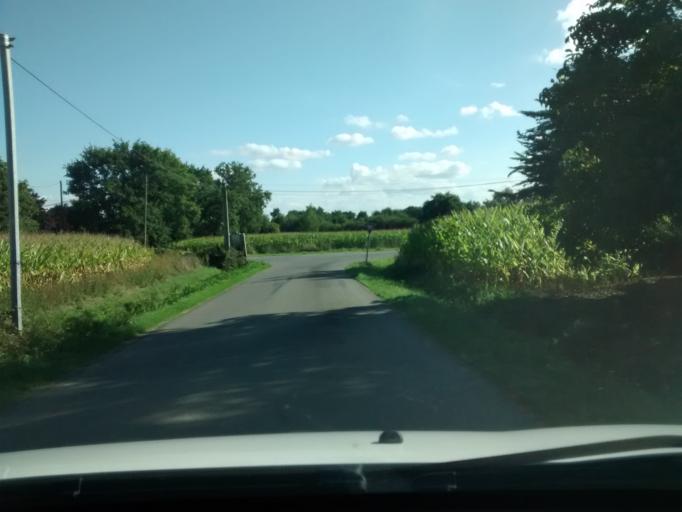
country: FR
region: Brittany
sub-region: Departement d'Ille-et-Vilaine
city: Vern-sur-Seiche
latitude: 48.0750
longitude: -1.5768
